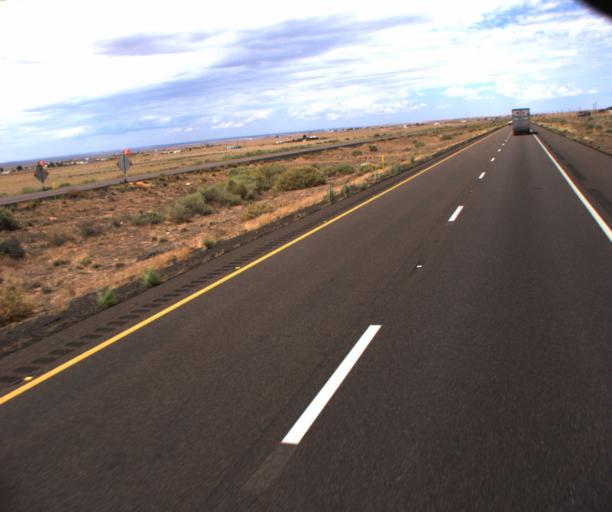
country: US
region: Arizona
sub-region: Navajo County
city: Holbrook
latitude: 34.9861
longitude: -110.0249
